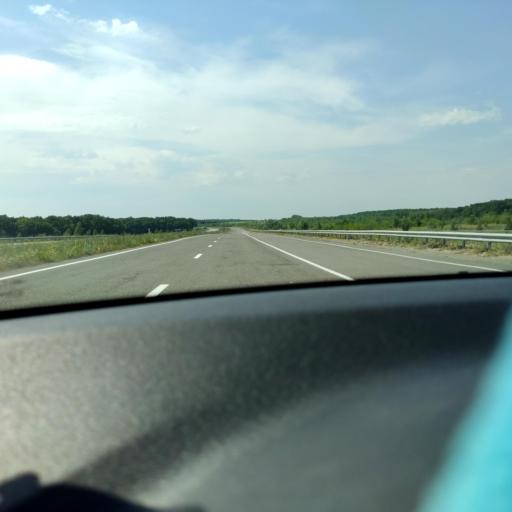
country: RU
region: Samara
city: Petra-Dubrava
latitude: 53.3396
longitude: 50.4496
